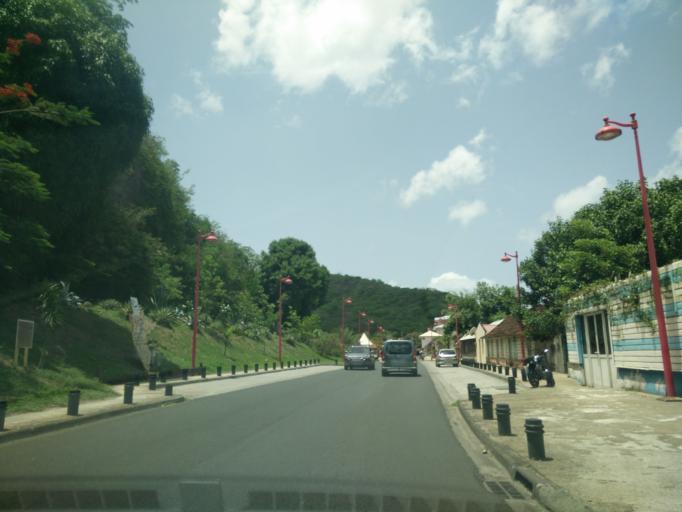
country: MQ
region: Martinique
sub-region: Martinique
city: Saint-Pierre
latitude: 14.7003
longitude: -61.1808
